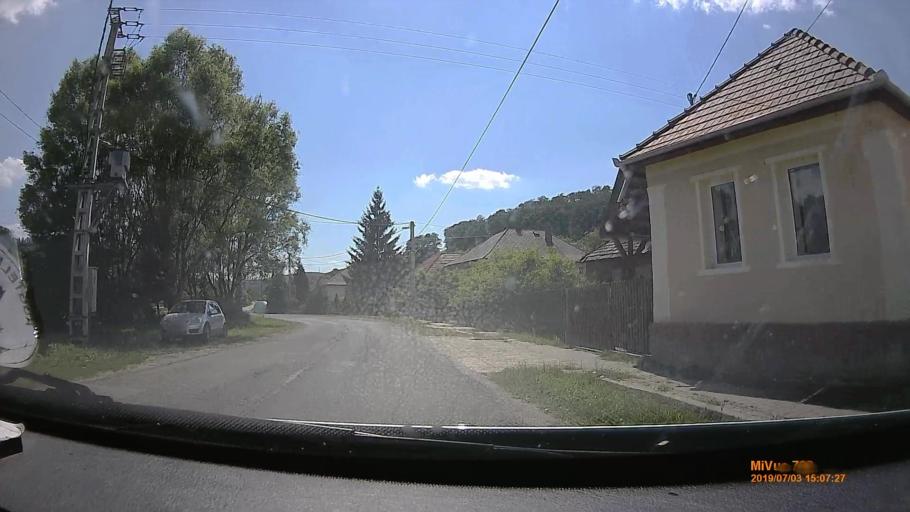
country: HU
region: Borsod-Abauj-Zemplen
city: Putnok
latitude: 48.2516
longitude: 20.3906
